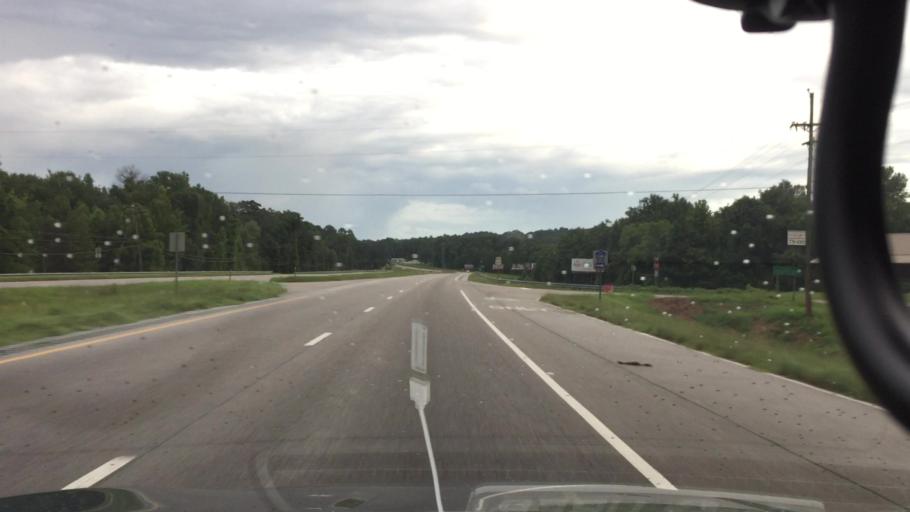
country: US
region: Alabama
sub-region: Pike County
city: Troy
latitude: 31.8483
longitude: -85.9954
